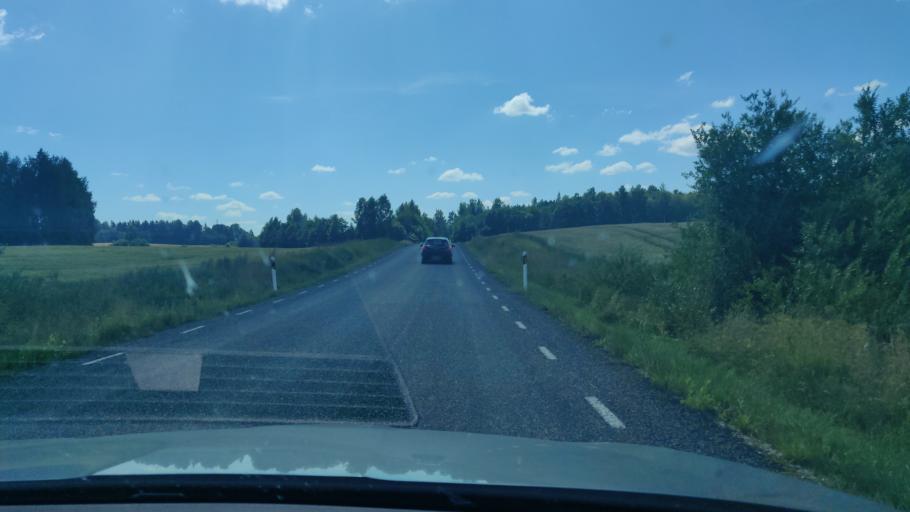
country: EE
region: Tartu
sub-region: Elva linn
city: Elva
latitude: 58.1449
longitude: 26.4755
